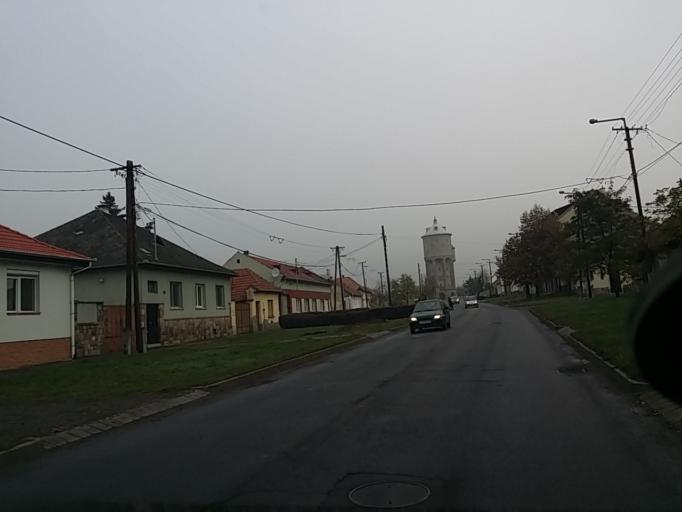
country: HU
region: Heves
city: Gyongyos
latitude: 47.7917
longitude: 19.9281
